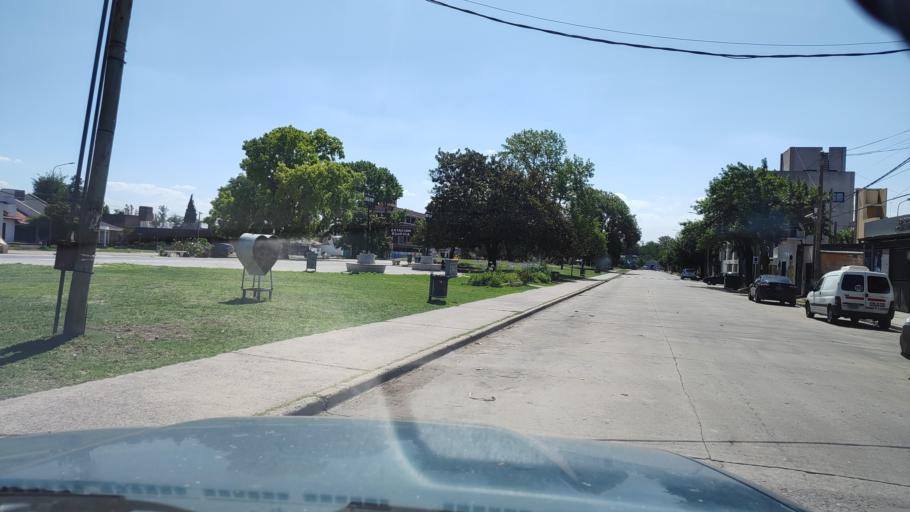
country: AR
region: Buenos Aires
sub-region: Partido de Lujan
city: Lujan
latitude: -34.5711
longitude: -59.1182
